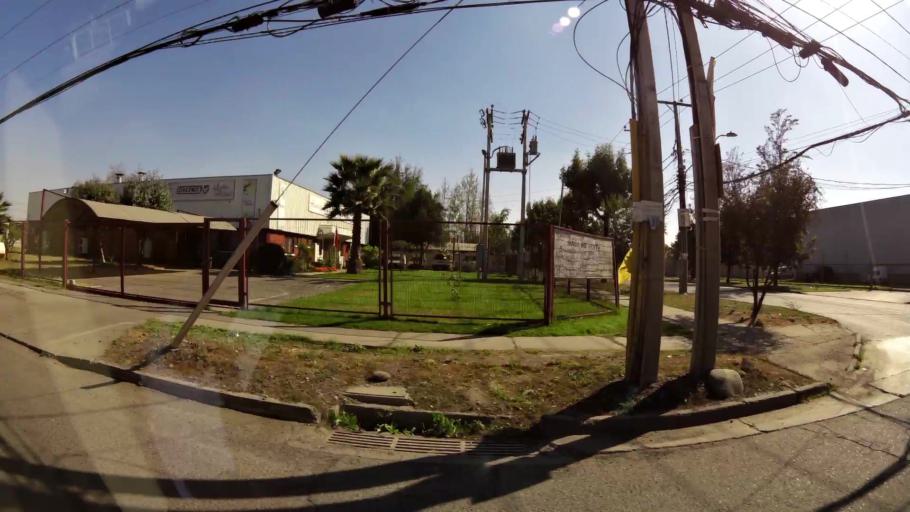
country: CL
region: Santiago Metropolitan
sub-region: Provincia de Chacabuco
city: Chicureo Abajo
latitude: -33.3298
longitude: -70.7070
